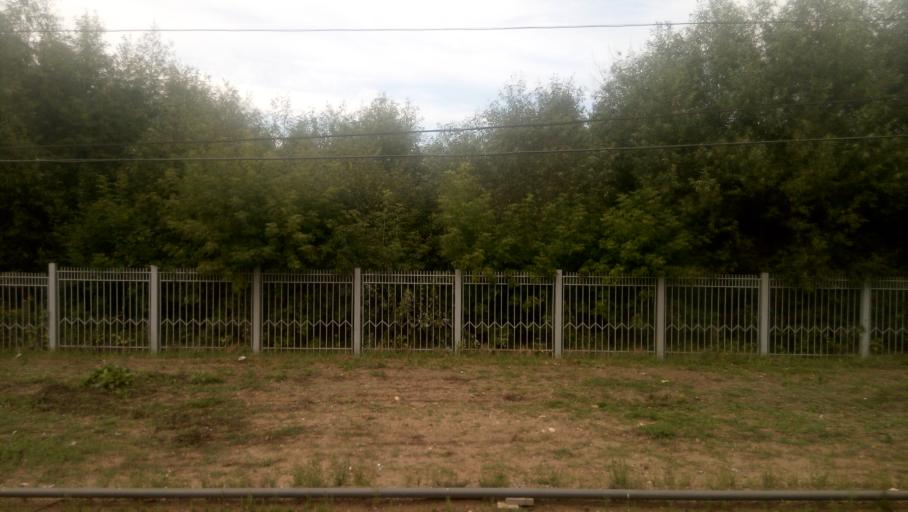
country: RU
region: Moskovskaya
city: Drezna
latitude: 55.7481
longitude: 38.8530
